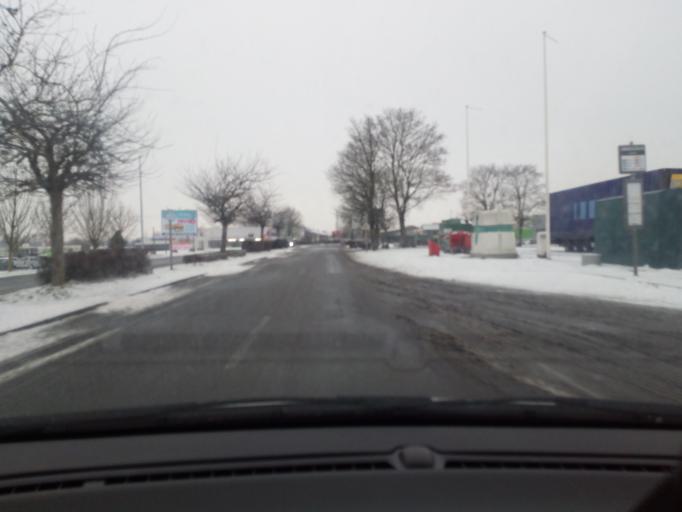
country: FR
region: Nord-Pas-de-Calais
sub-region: Departement du Nord
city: Hautmont
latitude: 50.2555
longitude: 3.9357
